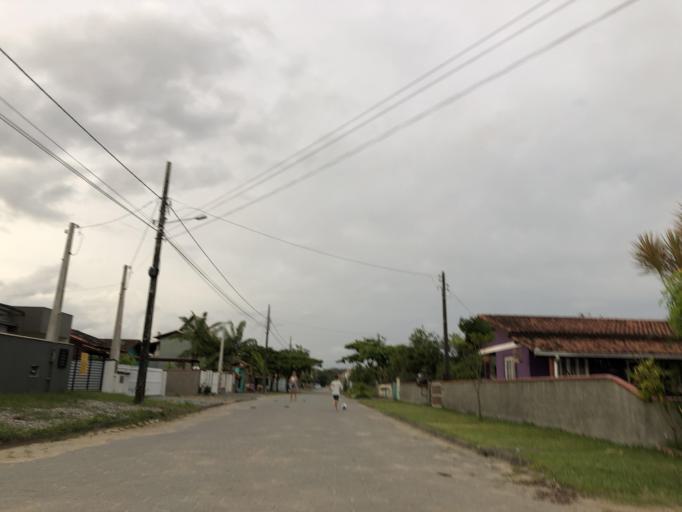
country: BR
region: Santa Catarina
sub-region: Sao Francisco Do Sul
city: Sao Francisco do Sul
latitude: -26.2133
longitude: -48.5296
